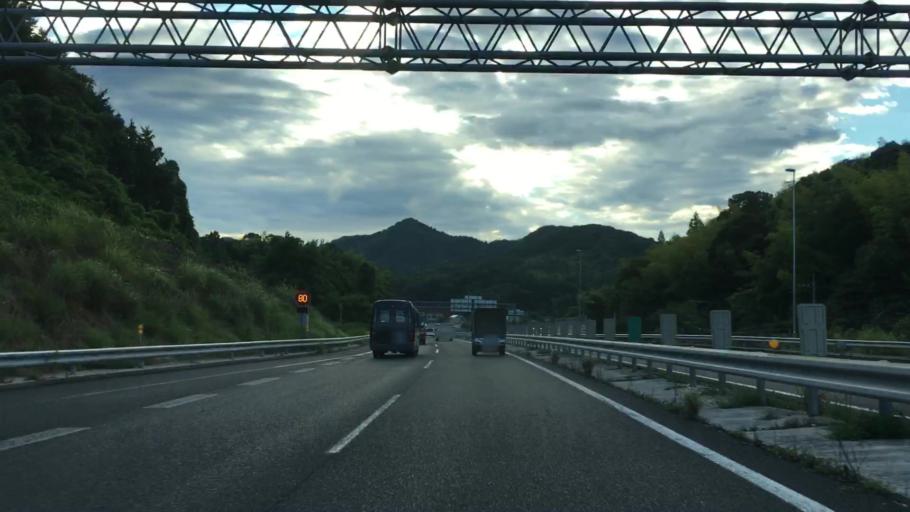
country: JP
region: Yamaguchi
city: Ogori-shimogo
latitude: 34.1728
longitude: 131.3183
